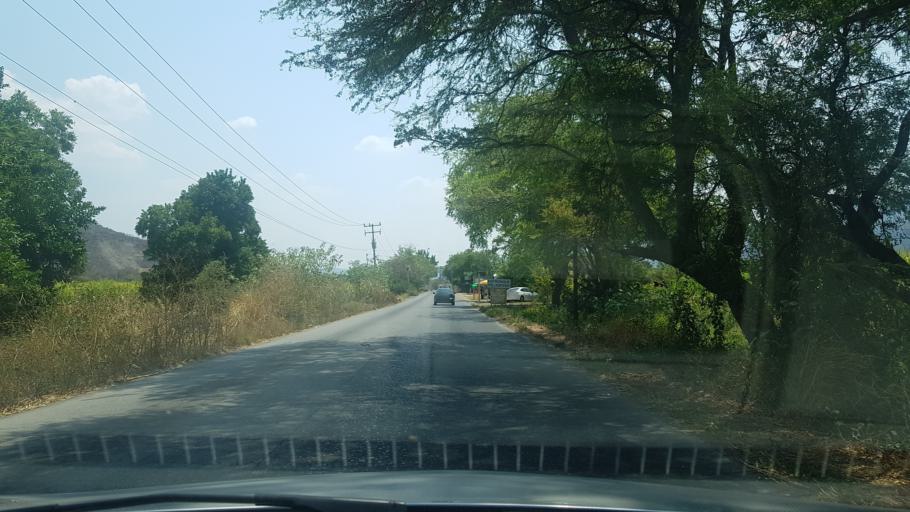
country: MX
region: Morelos
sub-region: Jiutepec
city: Independencia
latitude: 18.7982
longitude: -99.1017
